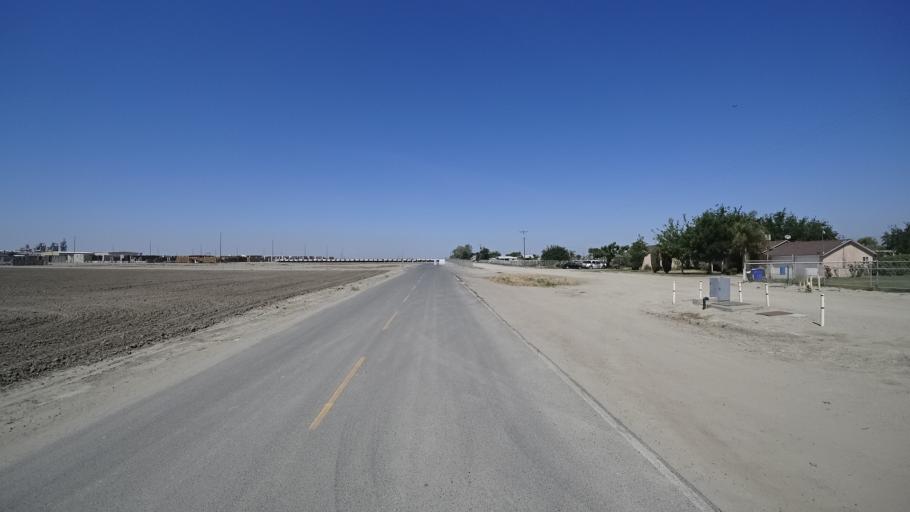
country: US
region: California
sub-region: Kings County
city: Corcoran
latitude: 36.0723
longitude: -119.5652
